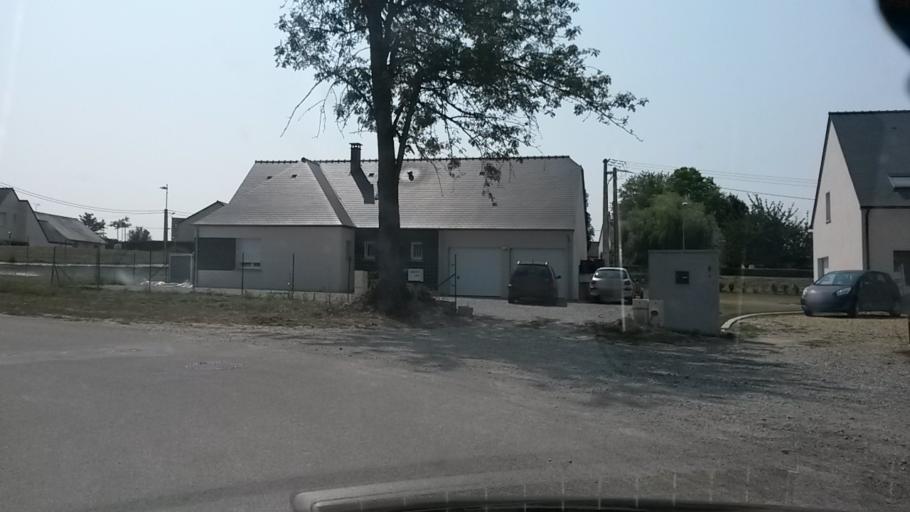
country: FR
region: Pays de la Loire
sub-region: Departement de la Mayenne
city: Soulge-sur-Ouette
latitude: 48.0192
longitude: -0.5853
